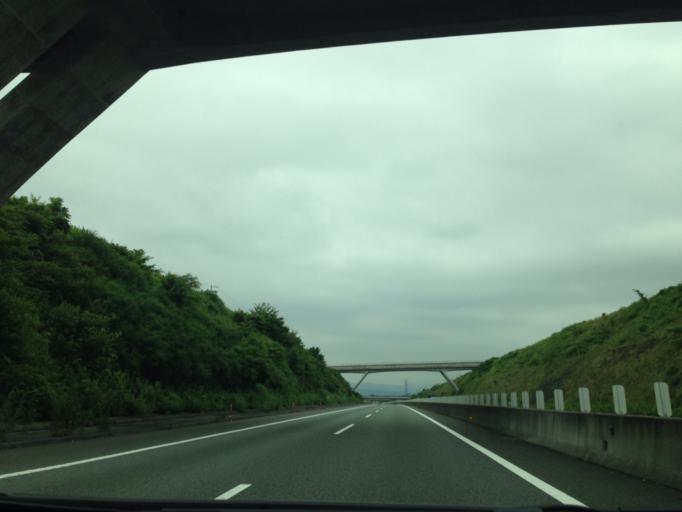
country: JP
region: Shizuoka
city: Fuji
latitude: 35.1987
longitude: 138.6931
